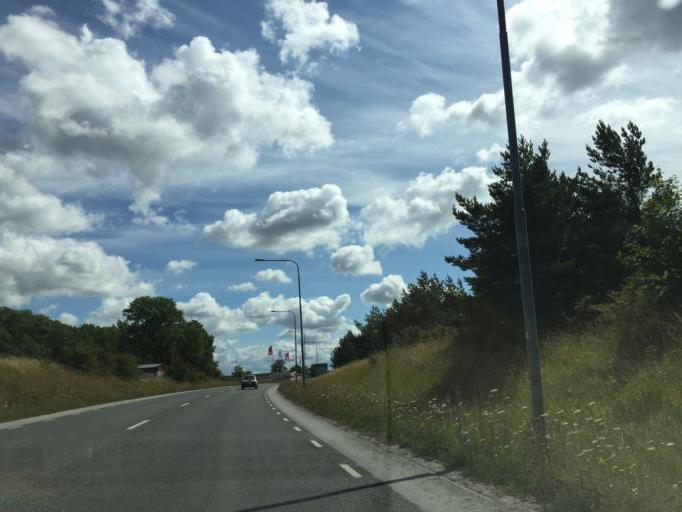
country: SE
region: Gotland
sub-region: Gotland
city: Visby
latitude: 57.6196
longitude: 18.2816
